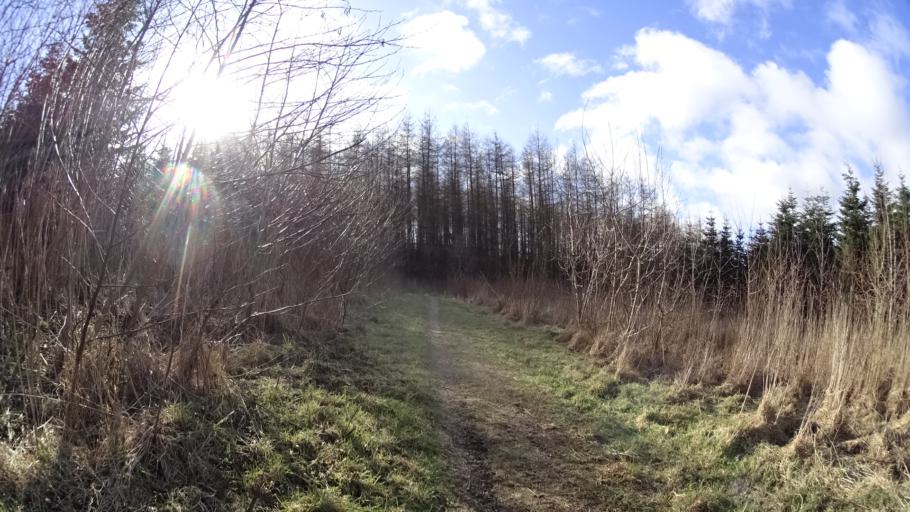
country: DK
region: Central Jutland
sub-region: Arhus Kommune
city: Tranbjerg
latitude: 56.1055
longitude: 10.1243
